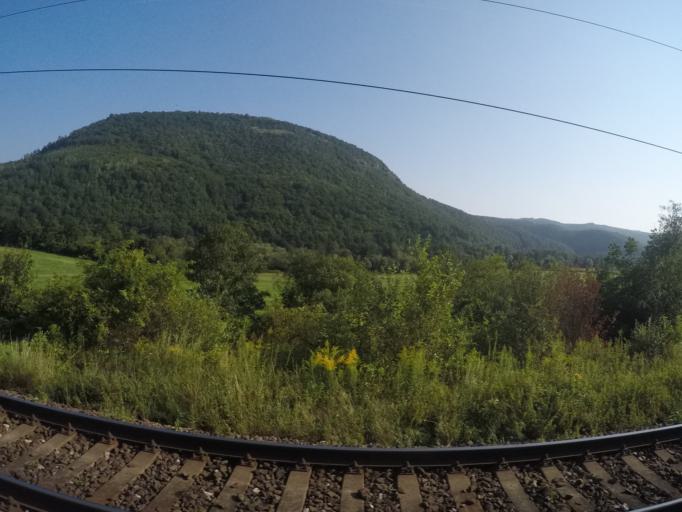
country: SK
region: Presovsky
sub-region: Okres Presov
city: Presov
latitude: 48.8515
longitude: 21.1710
